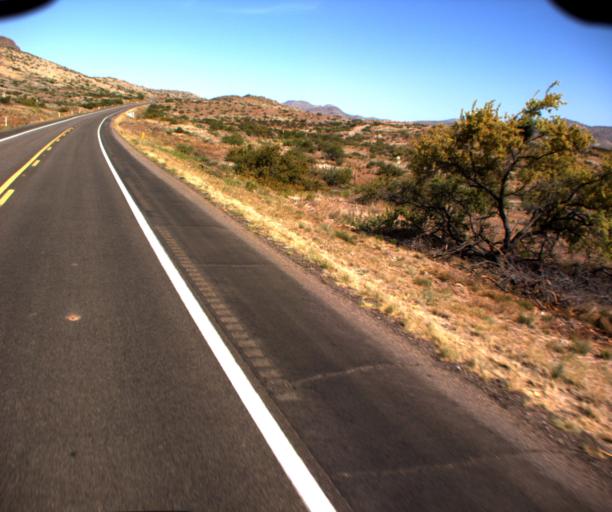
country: US
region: Arizona
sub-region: Greenlee County
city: Clifton
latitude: 32.7460
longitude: -109.2230
